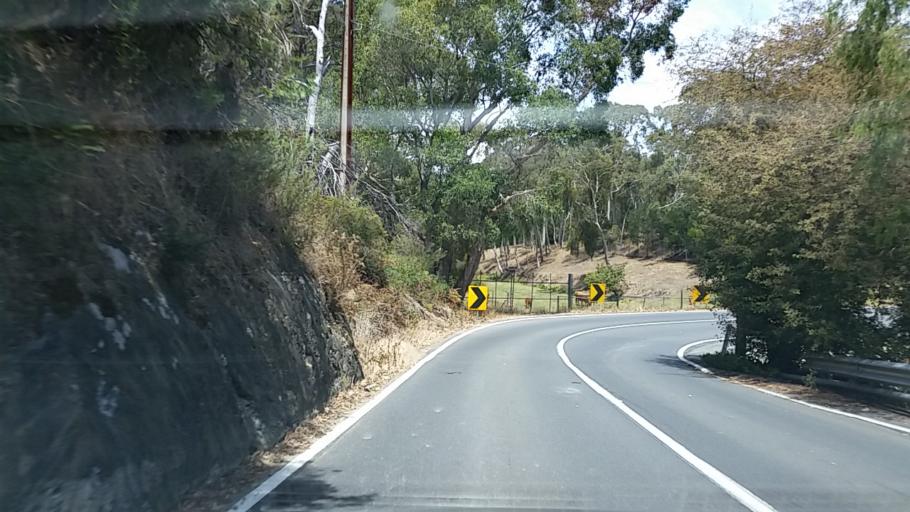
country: AU
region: South Australia
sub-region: Adelaide Hills
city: Upper Sturt
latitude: -35.0208
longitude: 138.6962
